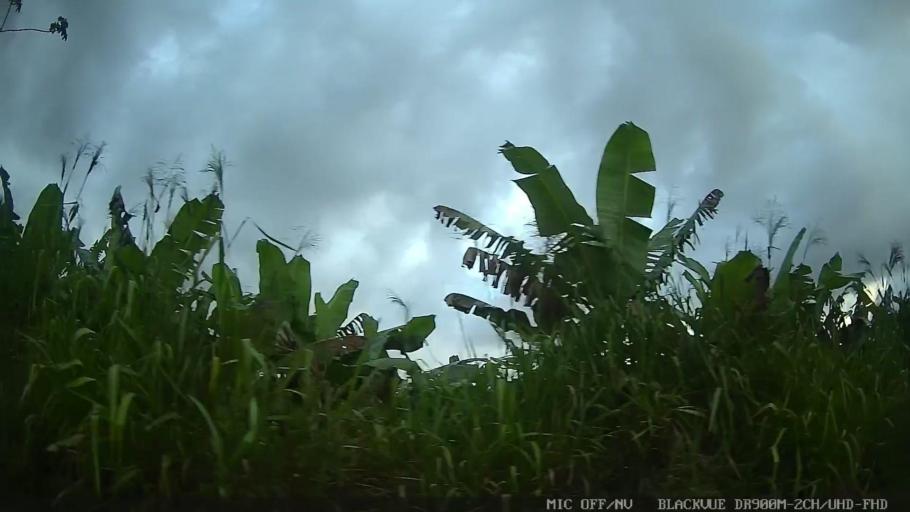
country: BR
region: Sao Paulo
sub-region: Itanhaem
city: Itanhaem
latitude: -24.0848
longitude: -46.8021
